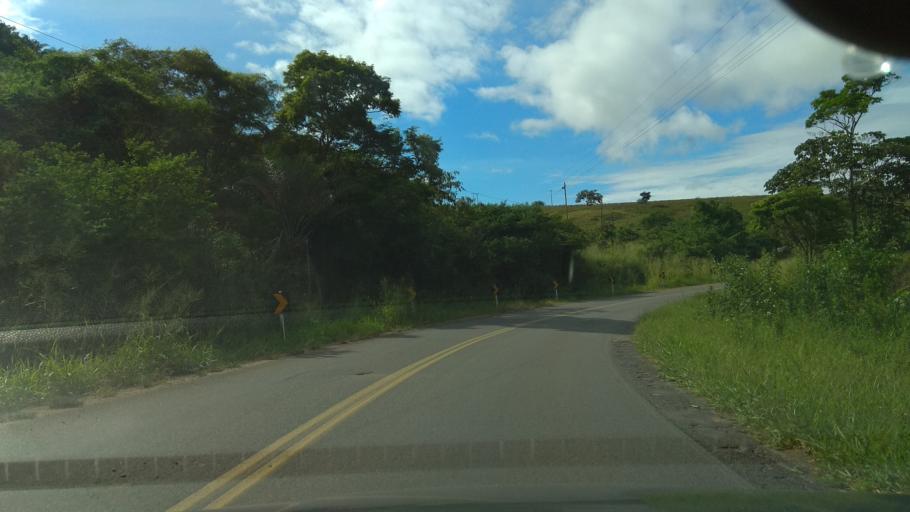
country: BR
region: Bahia
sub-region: Ubaira
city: Ubaira
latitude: -13.2599
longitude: -39.7024
